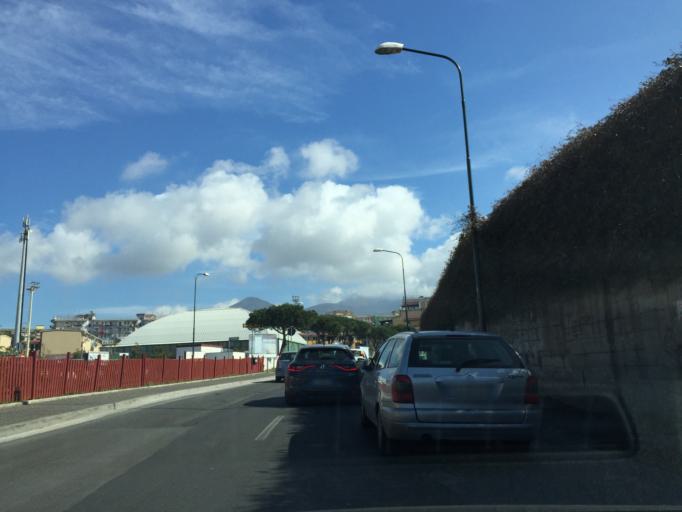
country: IT
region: Campania
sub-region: Provincia di Napoli
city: Portici
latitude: 40.8249
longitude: 14.3320
